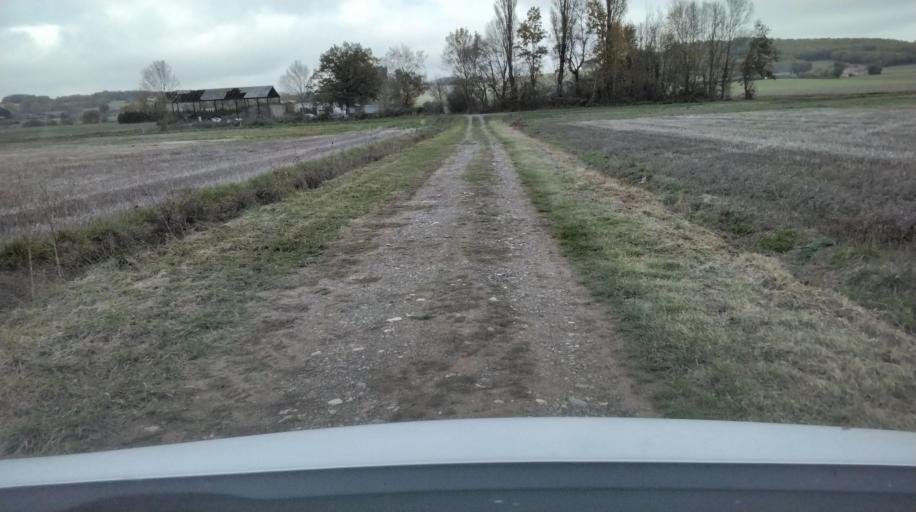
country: FR
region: Midi-Pyrenees
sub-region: Departement de la Haute-Garonne
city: Le Fousseret
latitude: 43.2684
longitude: 1.0316
